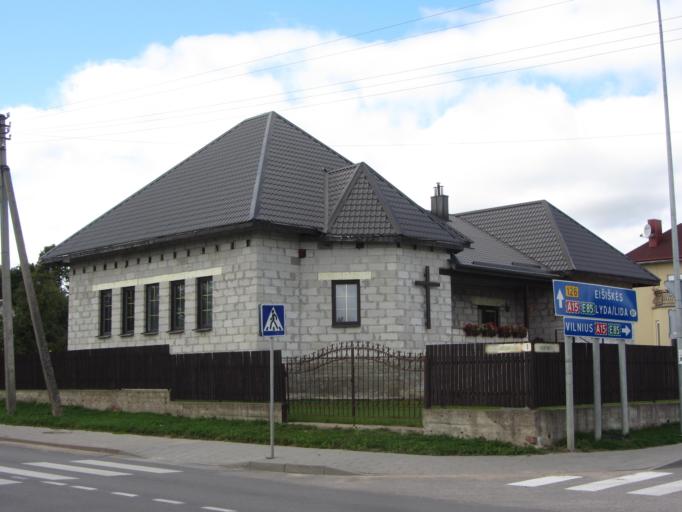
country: LT
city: Salcininkai
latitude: 54.3066
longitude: 25.3892
